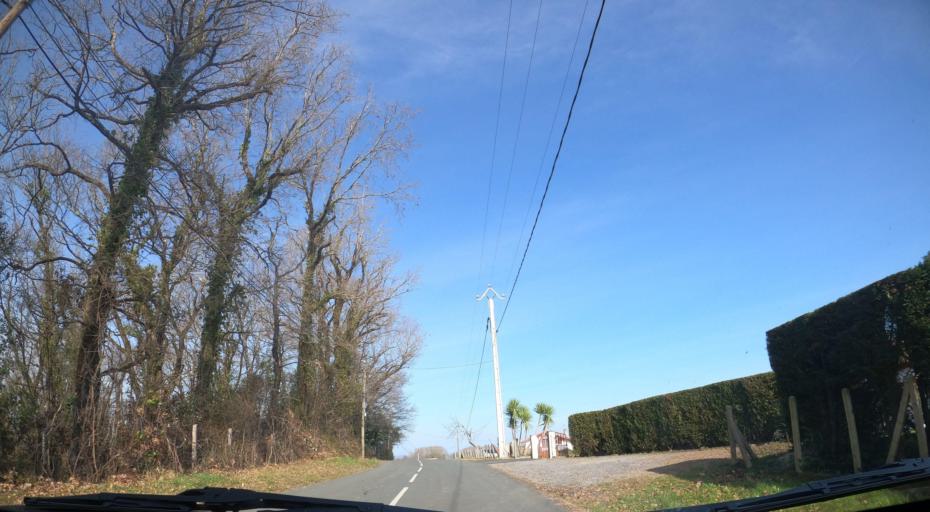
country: FR
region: Aquitaine
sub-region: Departement des Pyrenees-Atlantiques
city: Lahonce
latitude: 43.4362
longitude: -1.3782
